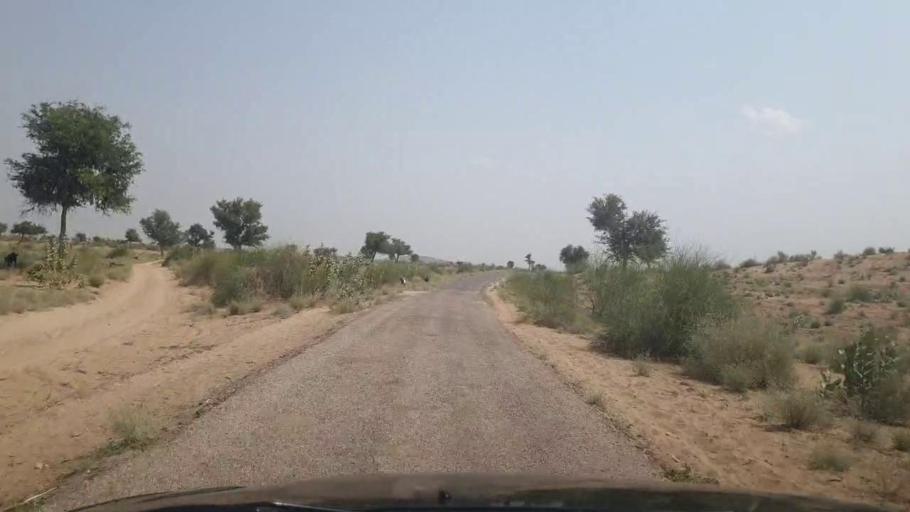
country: PK
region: Sindh
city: Islamkot
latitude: 25.0119
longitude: 70.3999
